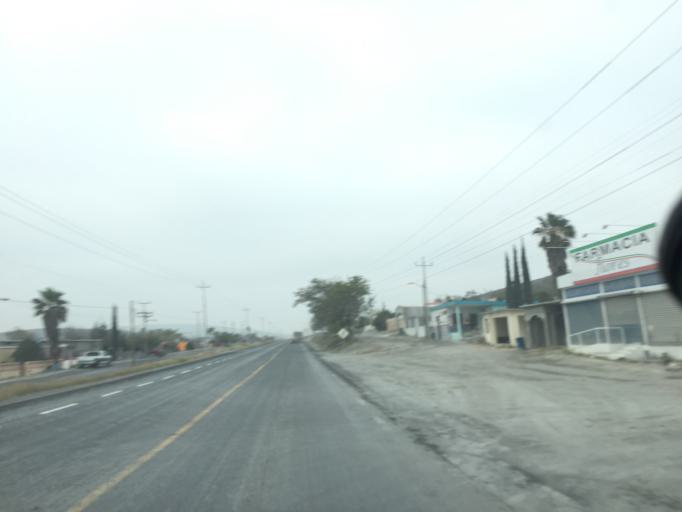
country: MX
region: Nuevo Leon
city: Mina
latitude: 26.0040
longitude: -100.5374
